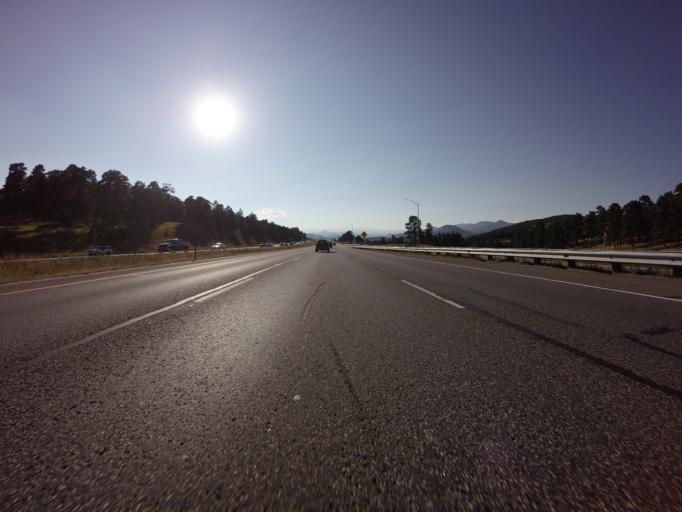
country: US
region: Colorado
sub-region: Jefferson County
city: Genesee
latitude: 39.7119
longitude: -105.3009
